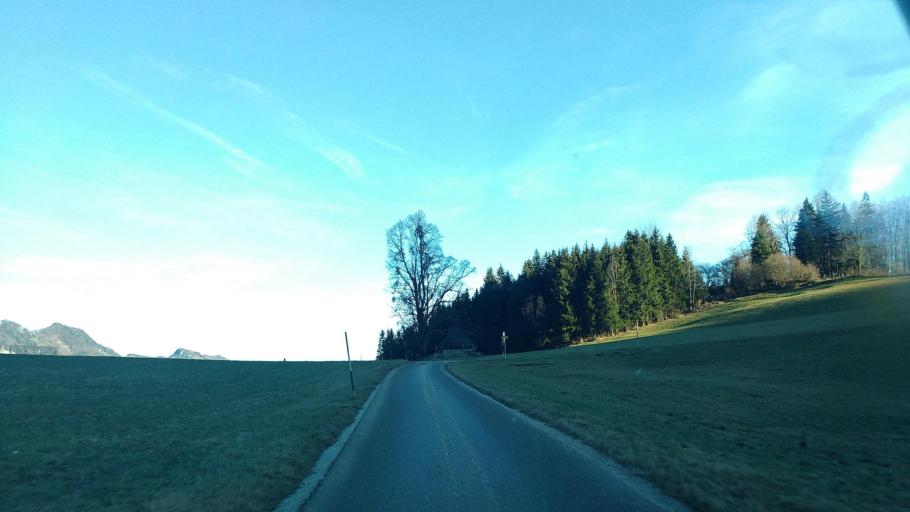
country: AT
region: Upper Austria
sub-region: Politischer Bezirk Kirchdorf an der Krems
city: Micheldorf in Oberoesterreich
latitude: 47.8971
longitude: 14.2118
